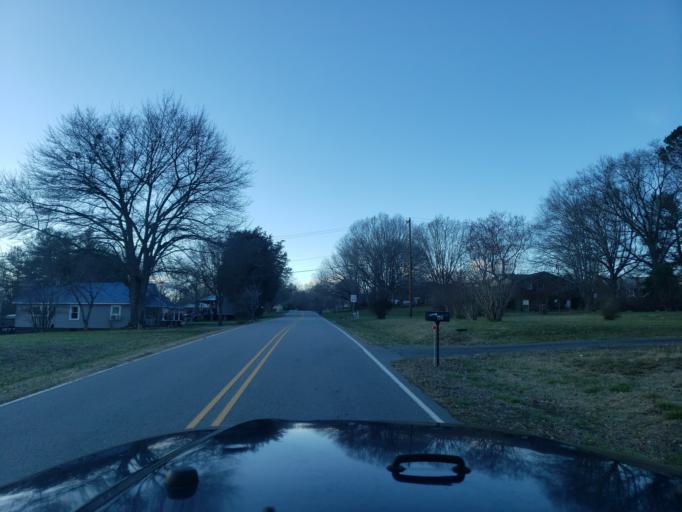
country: US
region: North Carolina
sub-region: Cleveland County
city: Shelby
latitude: 35.4153
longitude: -81.5665
